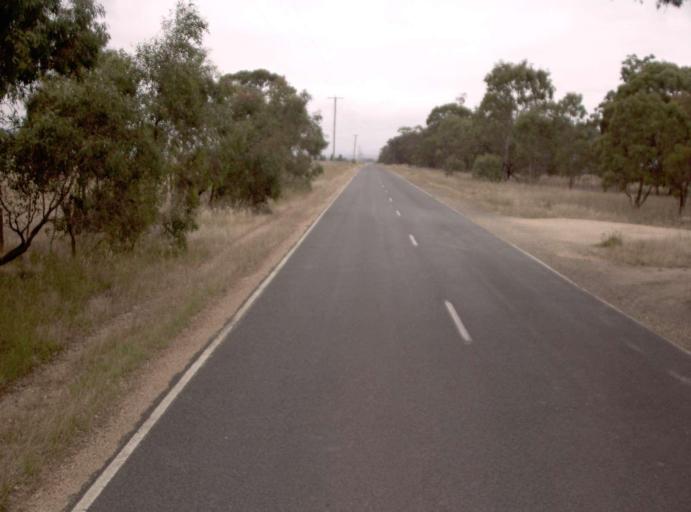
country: AU
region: Victoria
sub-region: Wellington
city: Heyfield
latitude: -38.0464
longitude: 146.7676
